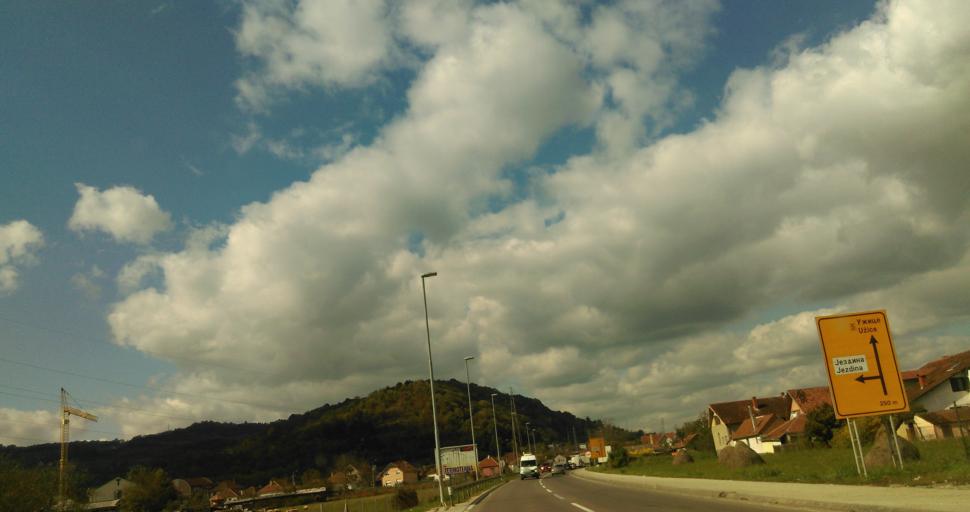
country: RS
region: Central Serbia
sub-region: Moravicki Okrug
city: Cacak
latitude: 43.8819
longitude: 20.3231
